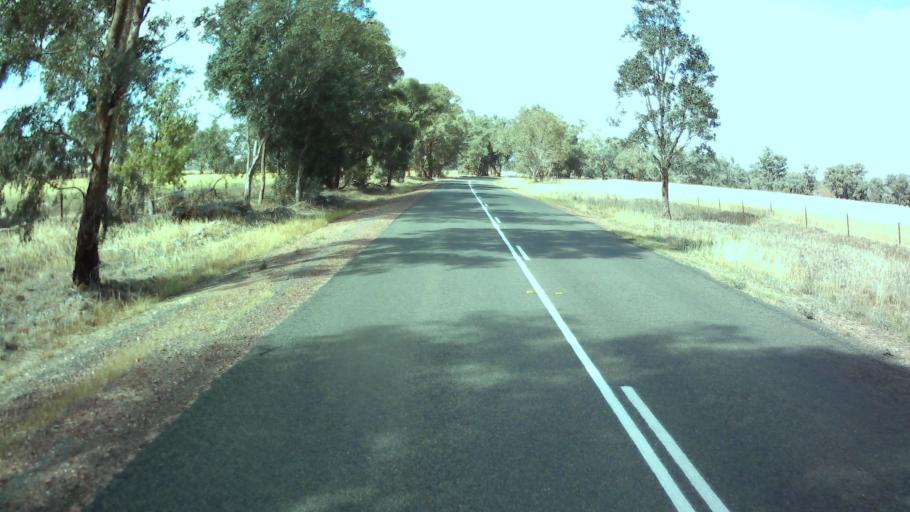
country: AU
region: New South Wales
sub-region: Weddin
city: Grenfell
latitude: -33.9837
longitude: 148.4161
